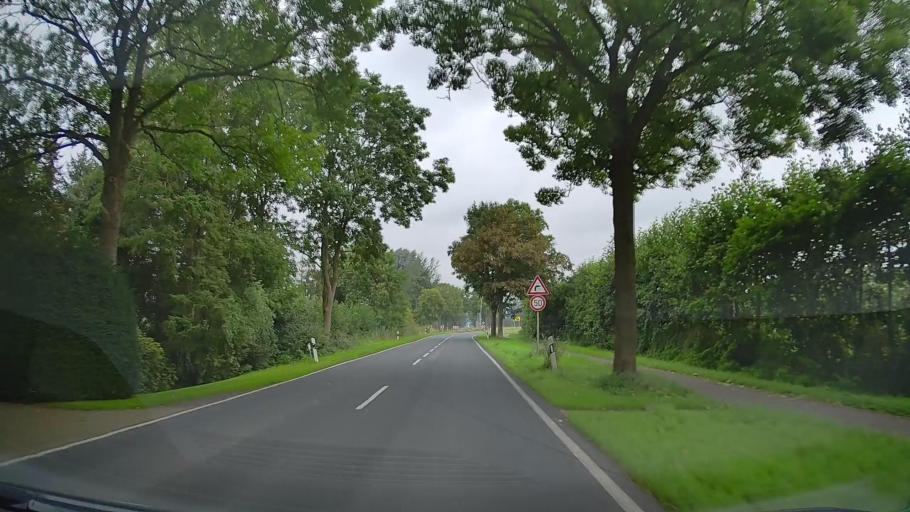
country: DE
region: Lower Saxony
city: Balje
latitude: 53.8208
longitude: 9.1317
